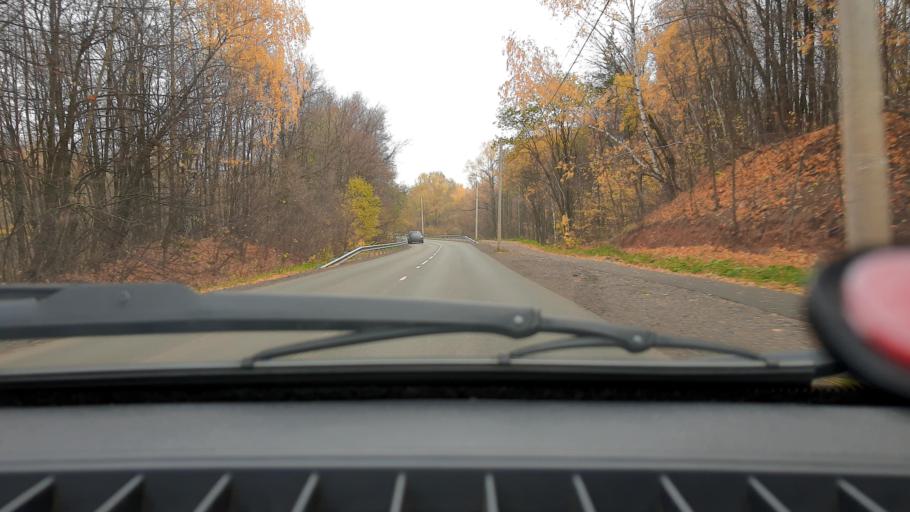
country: RU
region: Bashkortostan
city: Avdon
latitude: 54.6638
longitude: 55.7084
